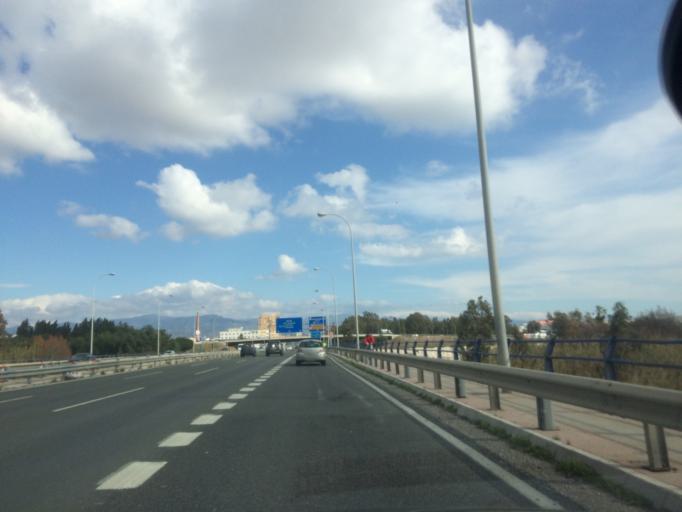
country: ES
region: Andalusia
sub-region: Provincia de Malaga
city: Torremolinos
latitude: 36.6786
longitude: -4.4727
